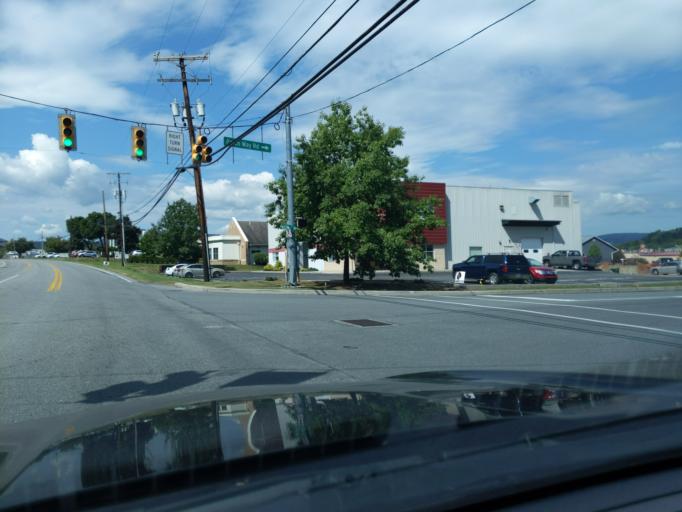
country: US
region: Pennsylvania
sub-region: Blair County
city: Duncansville
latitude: 40.4289
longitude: -78.4117
